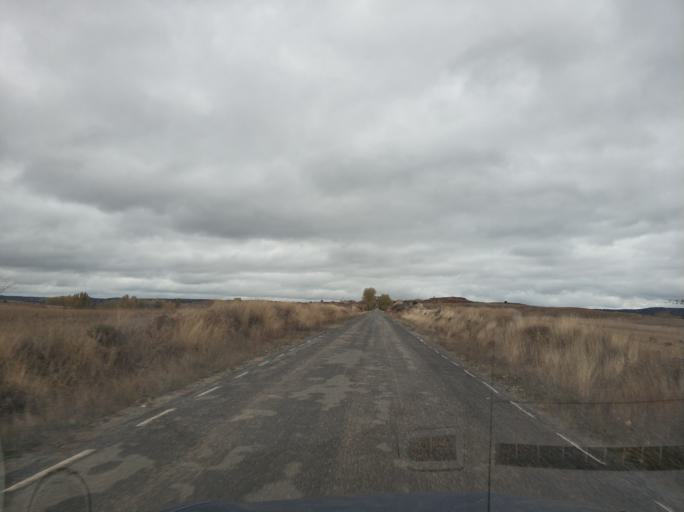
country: ES
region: Castille and Leon
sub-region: Provincia de Soria
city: San Esteban de Gormaz
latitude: 41.5908
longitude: -3.1782
